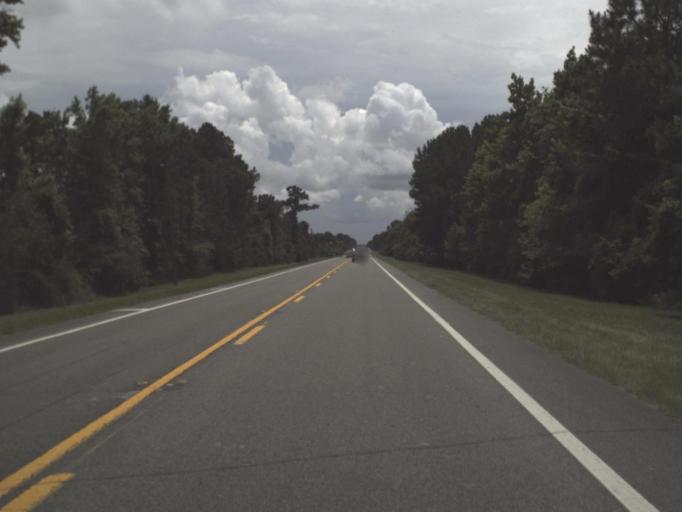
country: US
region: Florida
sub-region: Nassau County
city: Yulee
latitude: 30.5819
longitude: -81.6037
